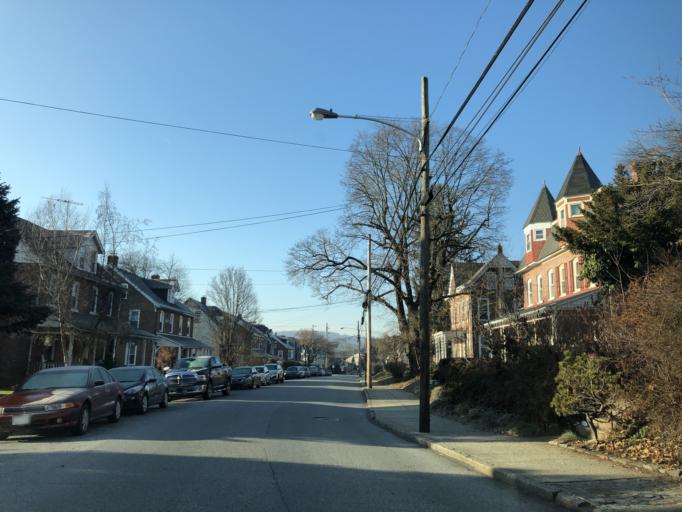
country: US
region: Pennsylvania
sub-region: Chester County
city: Downingtown
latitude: 40.0080
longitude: -75.6976
